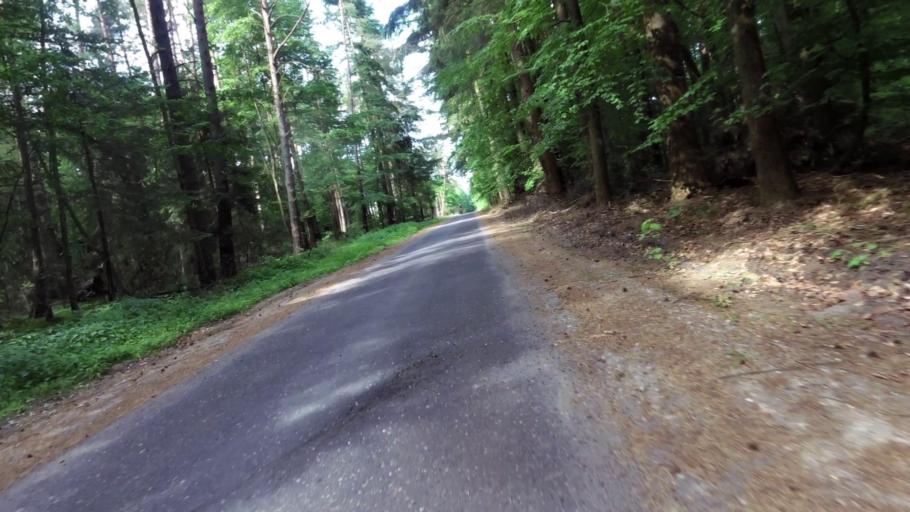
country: PL
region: West Pomeranian Voivodeship
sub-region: Powiat mysliborski
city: Debno
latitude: 52.8021
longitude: 14.6579
